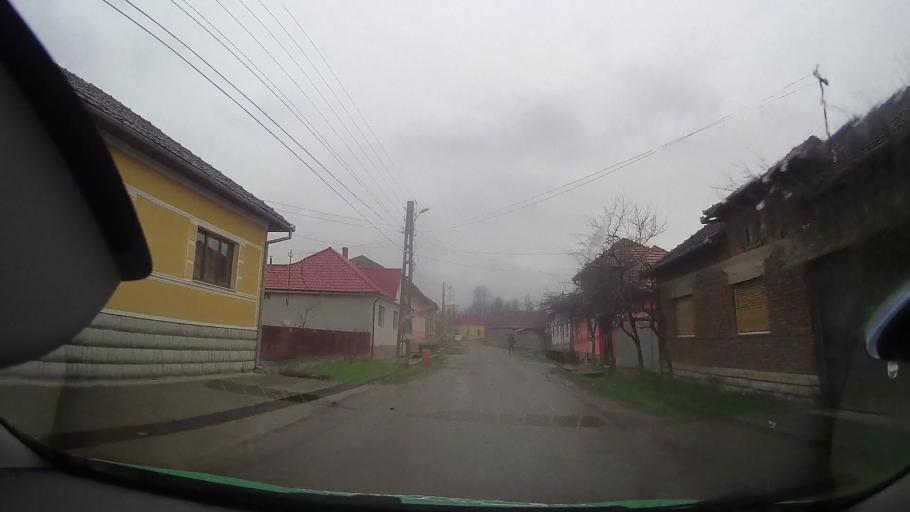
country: RO
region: Bihor
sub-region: Comuna Uileacu de Beius
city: Uileacu de Beius
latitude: 46.7093
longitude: 22.2257
